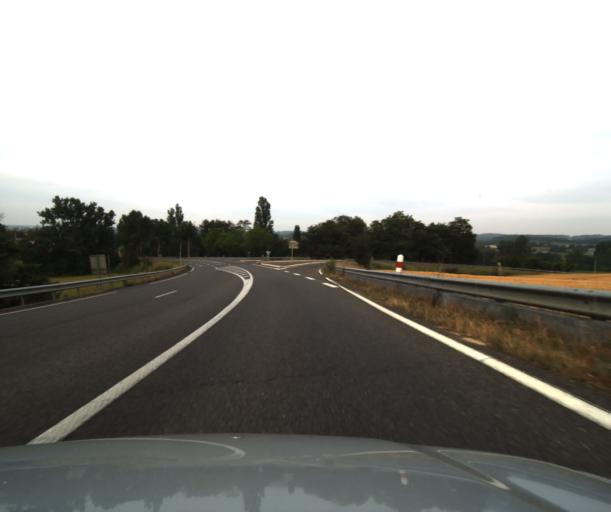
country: FR
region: Midi-Pyrenees
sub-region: Departement du Gers
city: Mirande
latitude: 43.5338
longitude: 0.4210
